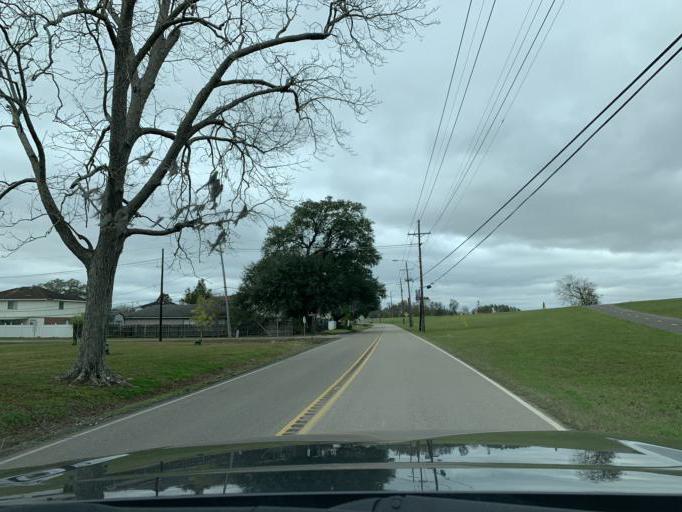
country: US
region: Louisiana
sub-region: Jefferson Parish
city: River Ridge
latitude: 29.9564
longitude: -90.2359
